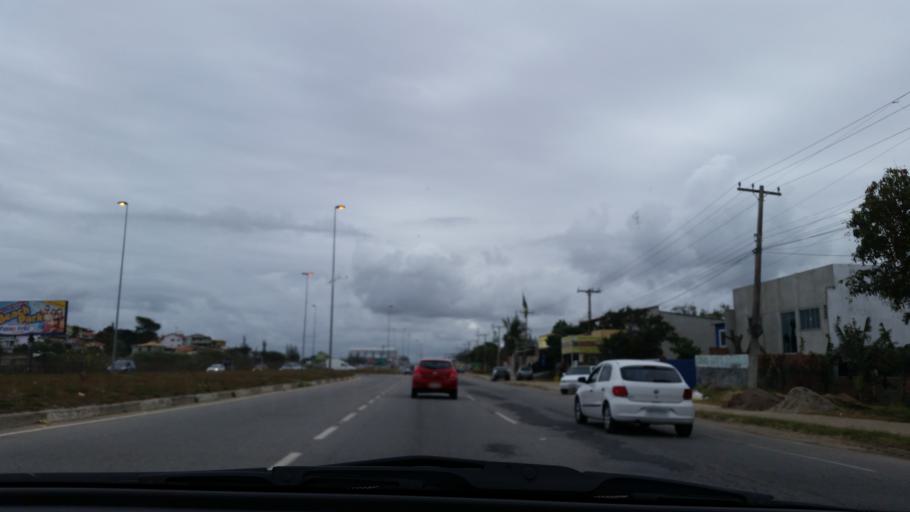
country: BR
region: Rio de Janeiro
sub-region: Sao Pedro Da Aldeia
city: Sao Pedro da Aldeia
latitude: -22.8459
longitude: -42.0671
